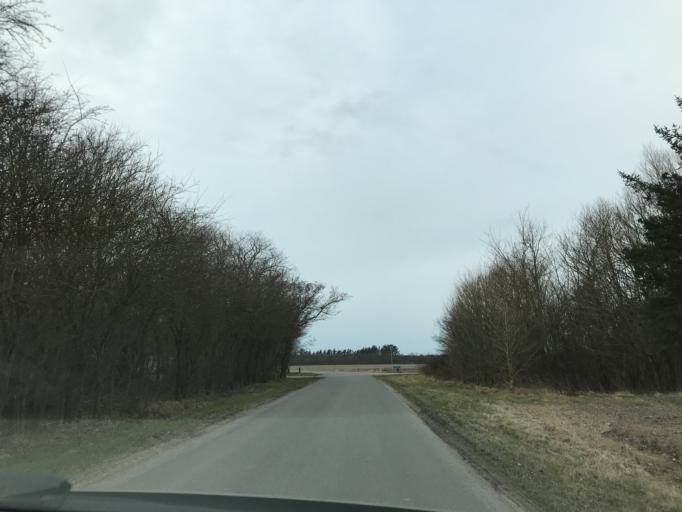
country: DK
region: South Denmark
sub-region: Varde Kommune
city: Oksbol
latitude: 55.8176
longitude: 8.2530
